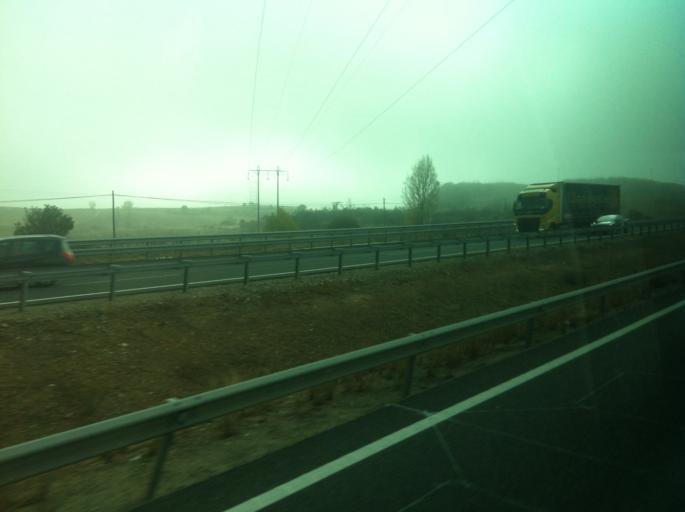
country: ES
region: Castille and Leon
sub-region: Provincia de Burgos
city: Saldana de Burgos
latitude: 42.2530
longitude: -3.7009
